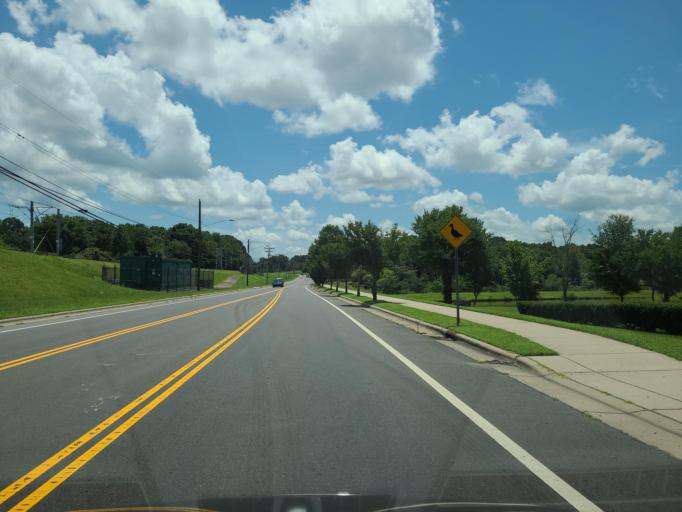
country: US
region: North Carolina
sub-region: Mecklenburg County
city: Pineville
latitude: 35.1510
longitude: -80.8783
